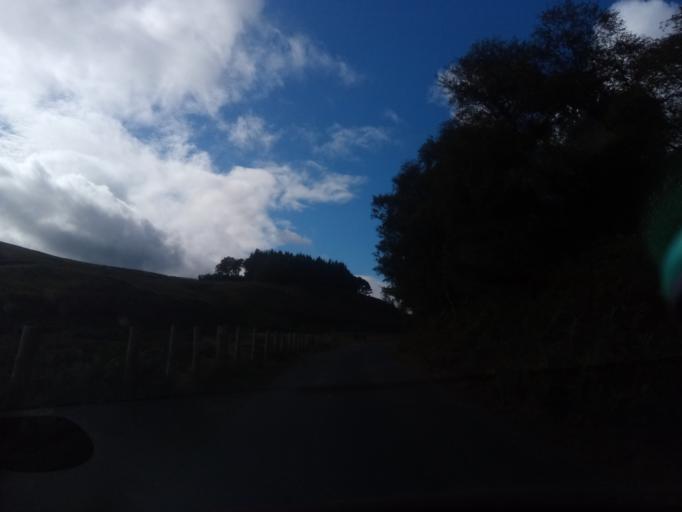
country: GB
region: Scotland
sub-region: East Lothian
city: Dunbar
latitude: 55.8621
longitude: -2.5296
